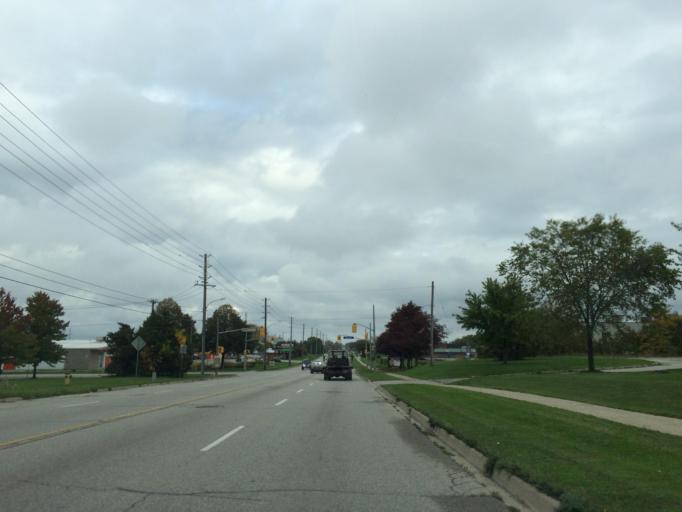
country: CA
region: Ontario
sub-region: Wellington County
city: Guelph
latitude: 43.5391
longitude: -80.2947
